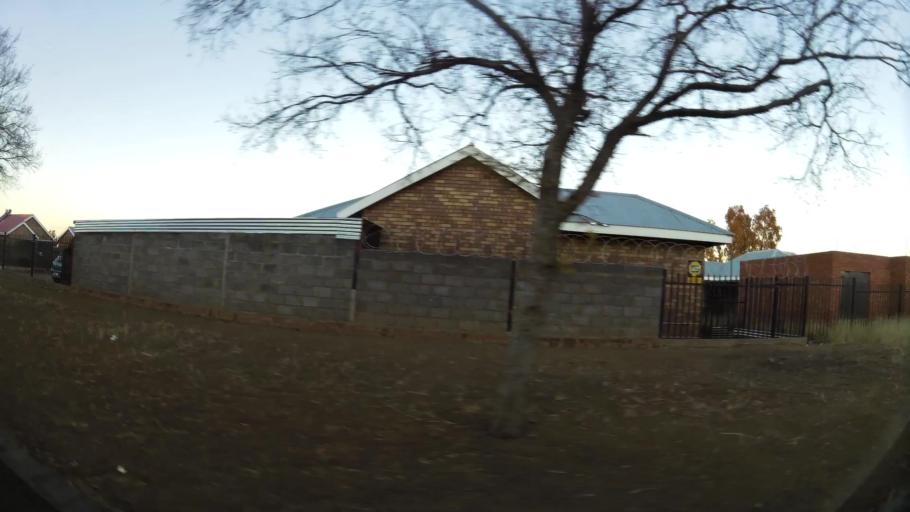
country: ZA
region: Northern Cape
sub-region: Frances Baard District Municipality
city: Kimberley
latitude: -28.7321
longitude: 24.7759
